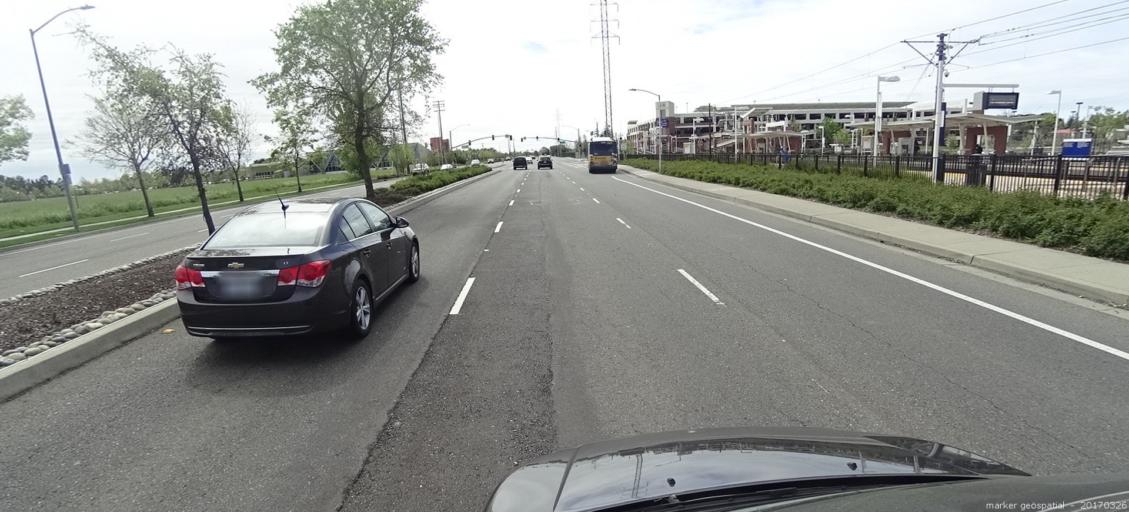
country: US
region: California
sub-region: Sacramento County
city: Laguna
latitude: 38.4543
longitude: -121.4180
